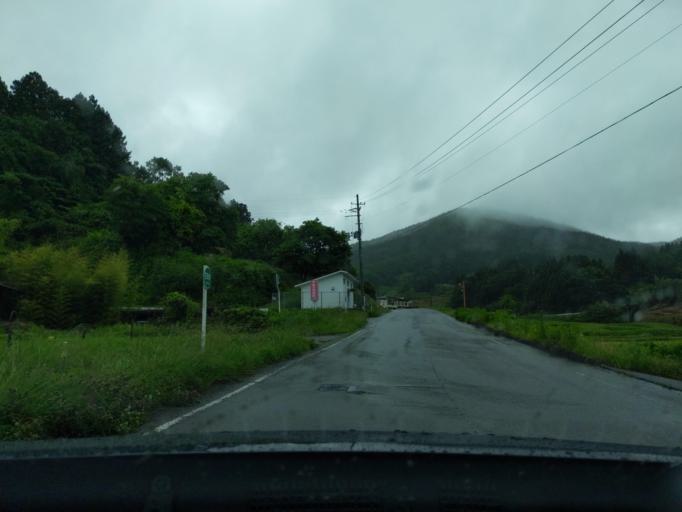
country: JP
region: Fukushima
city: Funehikimachi-funehiki
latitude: 37.5965
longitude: 140.5848
